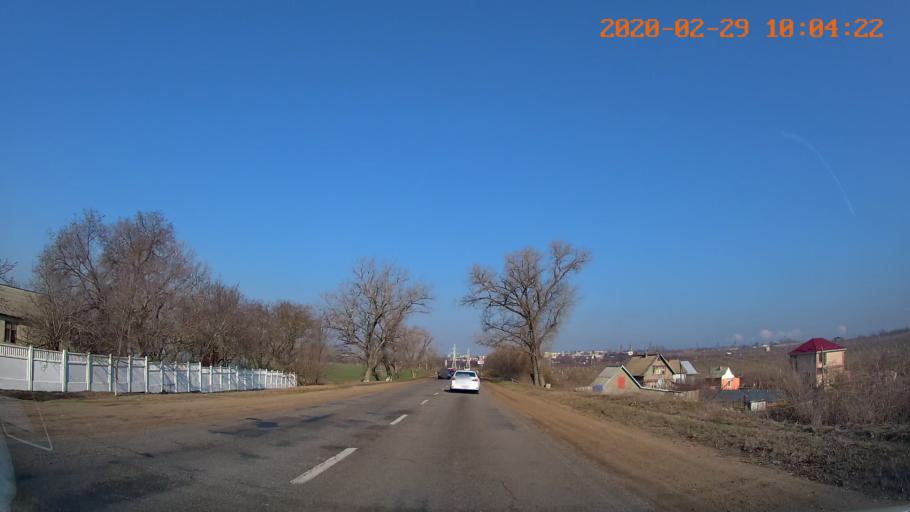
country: MD
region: Causeni
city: Chitcani
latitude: 46.7976
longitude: 29.6759
